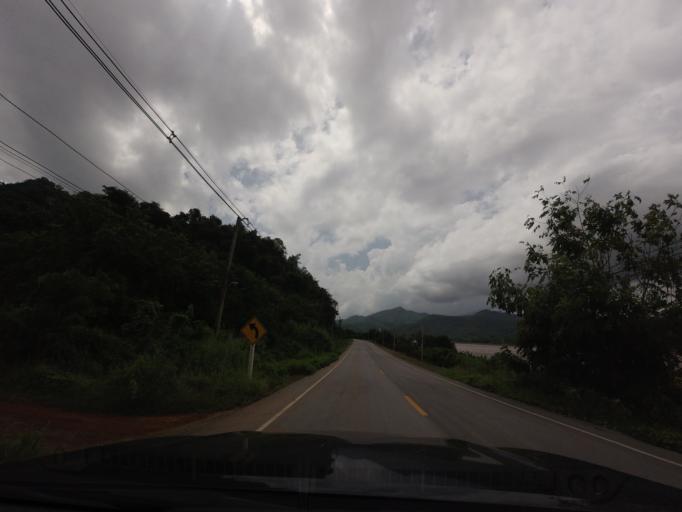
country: TH
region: Loei
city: Pak Chom
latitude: 18.0615
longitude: 101.7801
